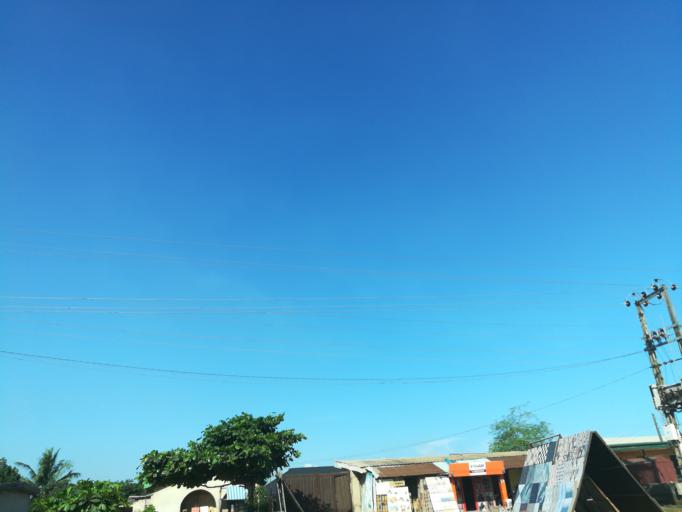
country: NG
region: Lagos
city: Ikorodu
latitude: 6.5776
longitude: 3.5266
